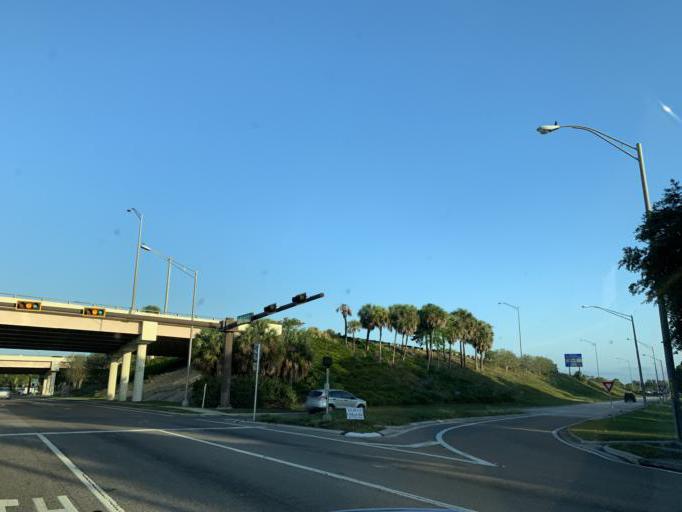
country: US
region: Florida
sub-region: Pinellas County
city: Lealman
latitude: 27.8066
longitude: -82.6615
